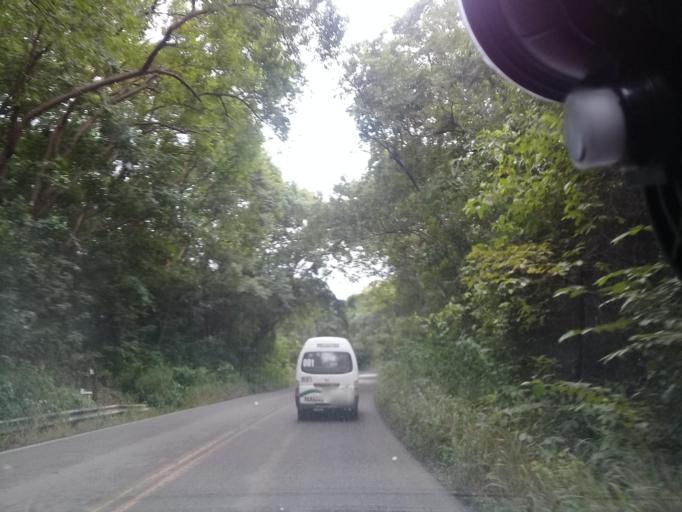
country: MX
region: Hidalgo
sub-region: Huejutla de Reyes
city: Parque de Poblamiento Solidaridad
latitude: 21.1988
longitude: -98.3889
